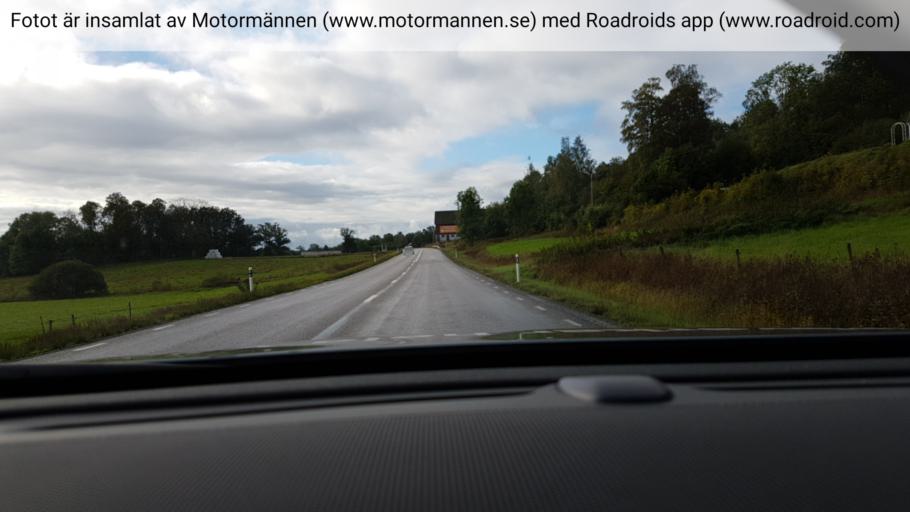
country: SE
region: Vaestra Goetaland
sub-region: Harryda Kommun
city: Ravlanda
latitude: 57.5406
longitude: 12.5323
